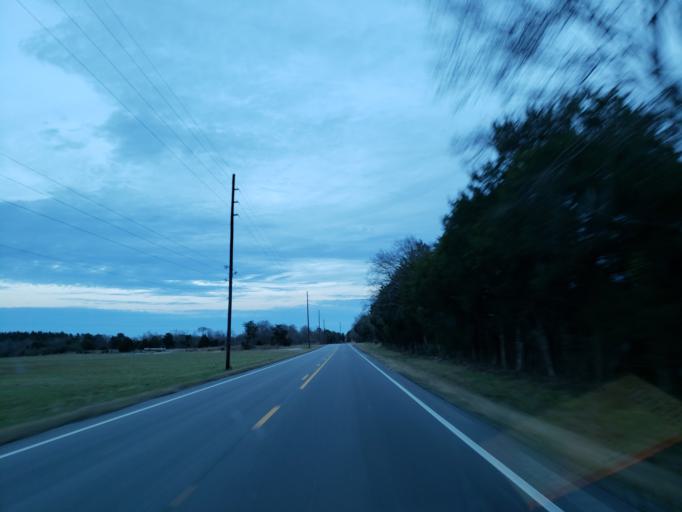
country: US
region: Alabama
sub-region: Sumter County
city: Livingston
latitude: 32.8110
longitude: -88.2845
